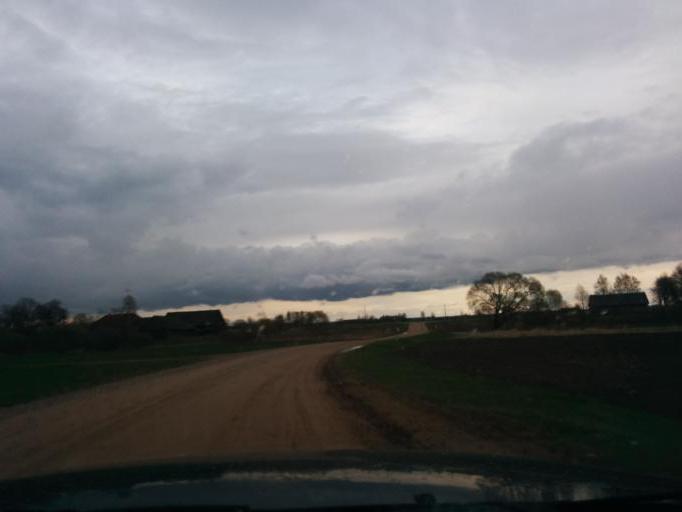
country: LT
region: Siauliu apskritis
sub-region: Joniskis
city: Joniskis
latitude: 56.3722
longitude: 23.5424
